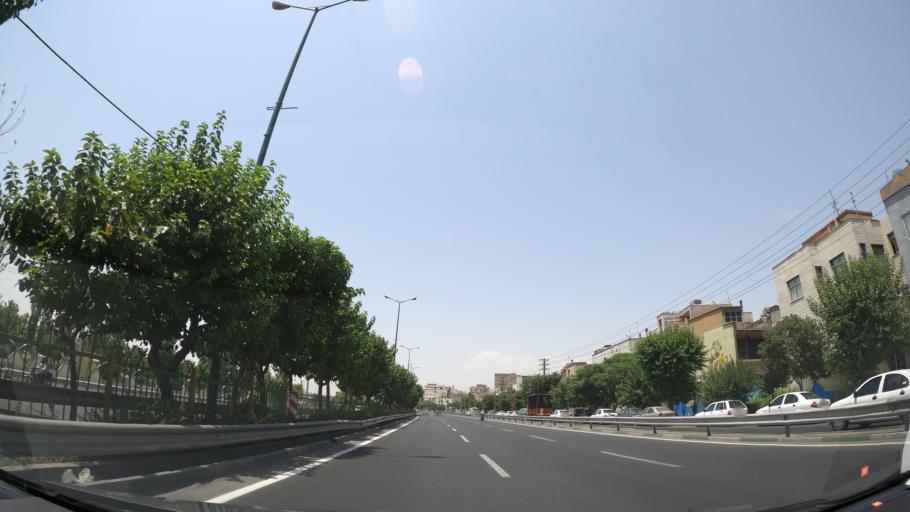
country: IR
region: Tehran
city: Tehran
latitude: 35.6496
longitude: 51.3893
